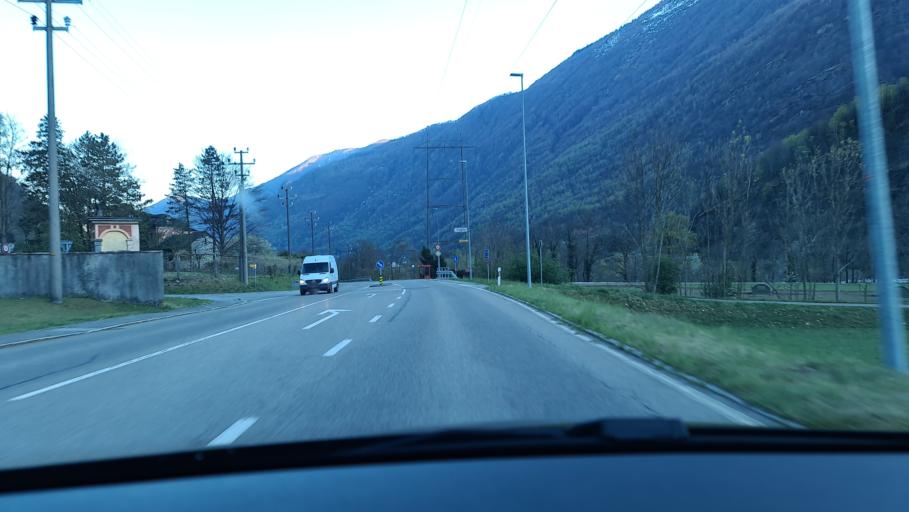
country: CH
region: Ticino
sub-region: Vallemaggia District
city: Cevio
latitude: 46.2698
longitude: 8.6827
